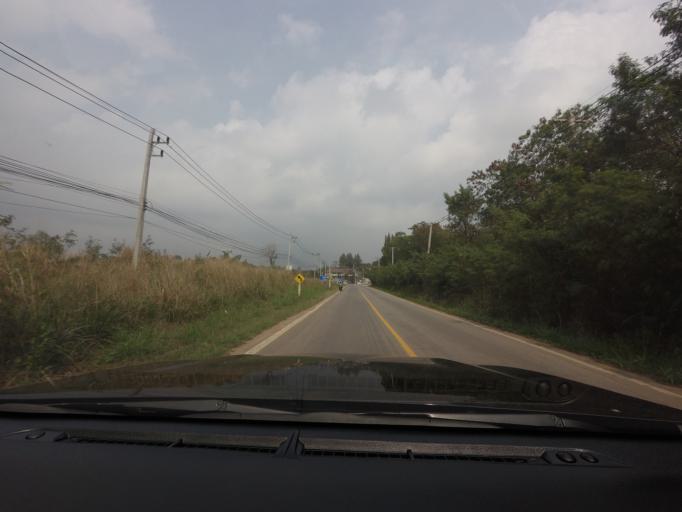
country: TH
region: Nakhon Ratchasima
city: Pak Chong
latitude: 14.4945
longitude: 101.5538
